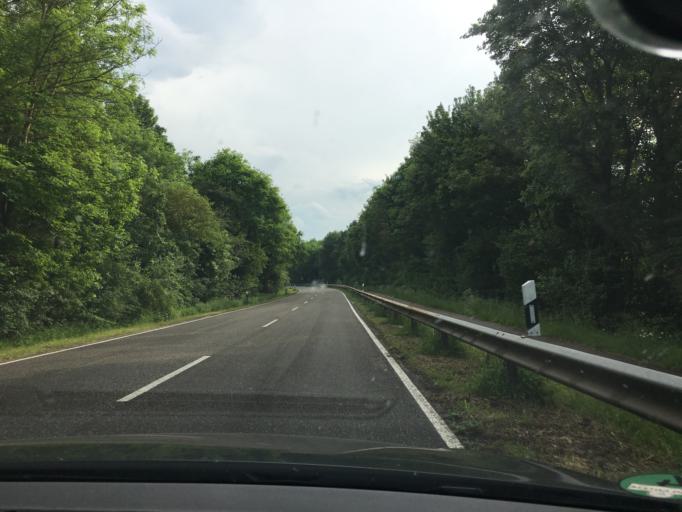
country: DE
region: North Rhine-Westphalia
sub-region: Regierungsbezirk Koln
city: Nideggen
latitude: 50.6727
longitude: 6.4827
